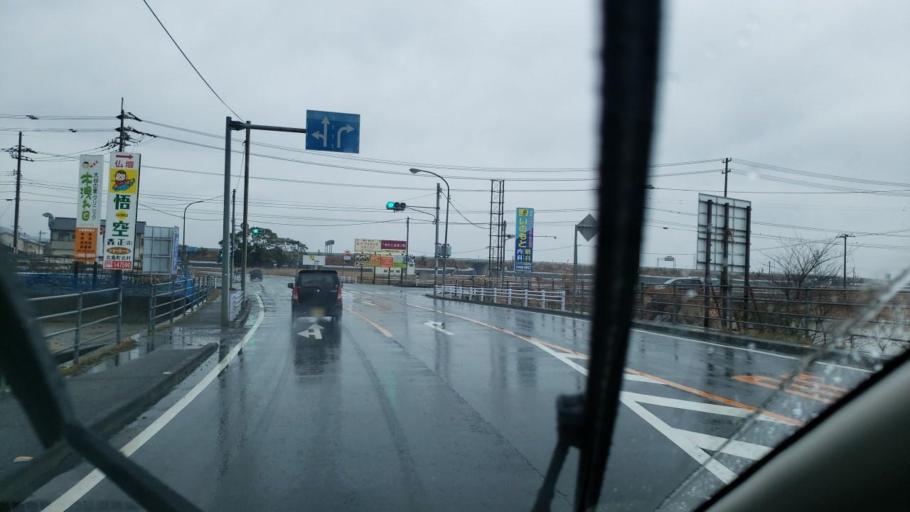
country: JP
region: Tokushima
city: Narutocho-mitsuishi
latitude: 34.1606
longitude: 134.5562
